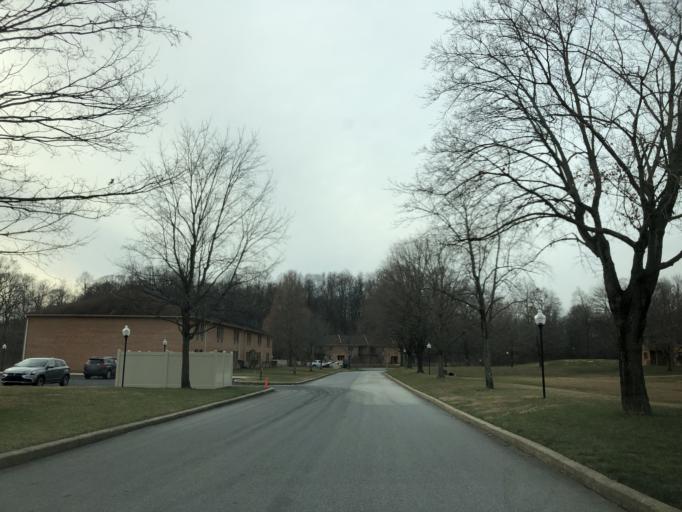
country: US
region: Pennsylvania
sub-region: Chester County
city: Exton
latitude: 40.0360
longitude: -75.6347
